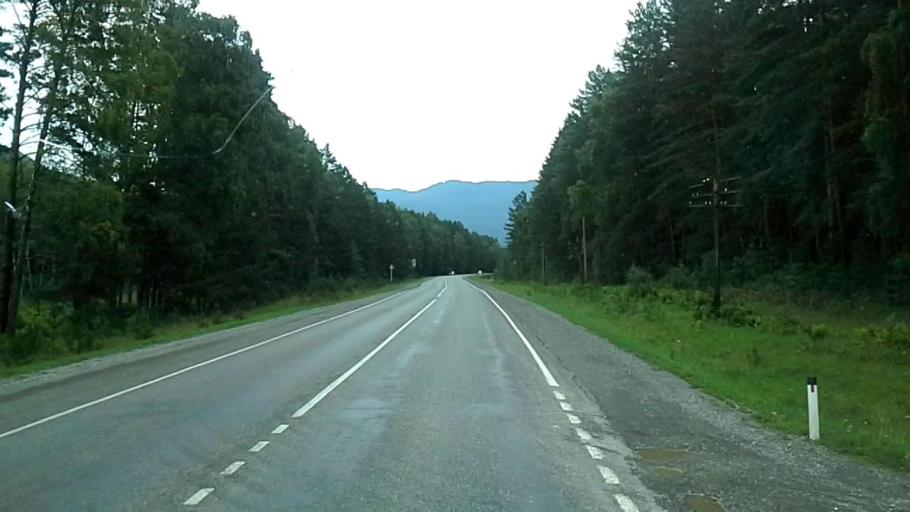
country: RU
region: Altay
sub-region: Mayminskiy Rayon
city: Manzherok
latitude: 51.8339
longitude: 85.7449
